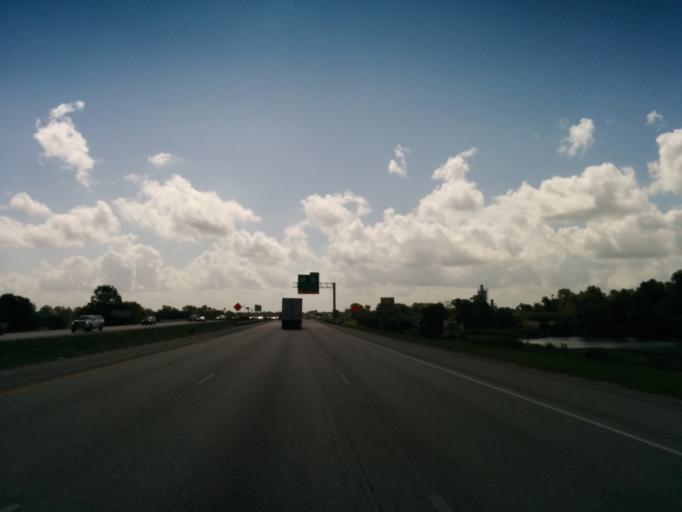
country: US
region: Texas
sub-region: Colorado County
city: Columbus
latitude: 29.6931
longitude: -96.5550
